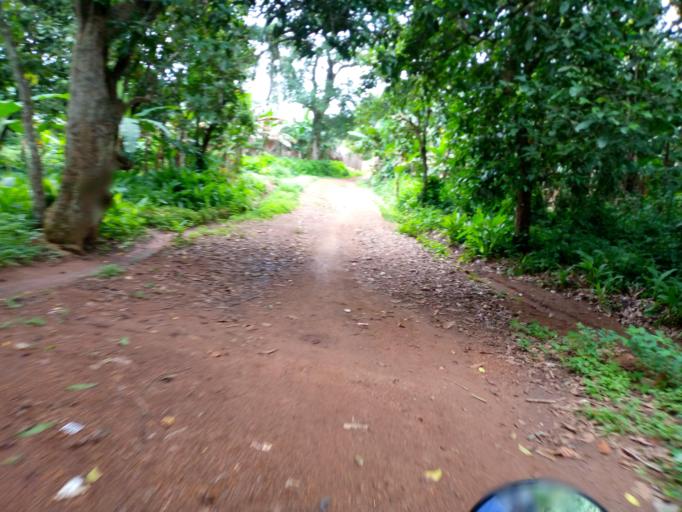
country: SL
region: Northern Province
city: Mange
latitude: 8.9780
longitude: -12.7093
